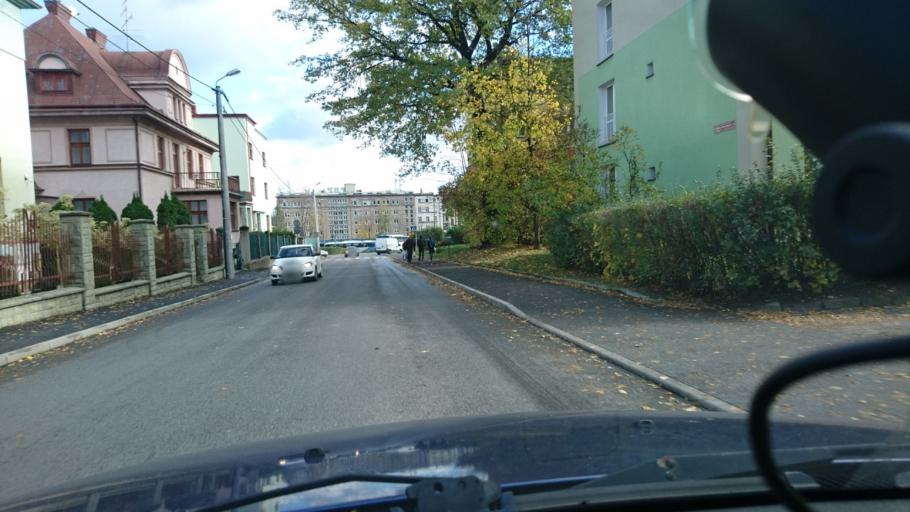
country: PL
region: Silesian Voivodeship
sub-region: Bielsko-Biala
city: Bielsko-Biala
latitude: 49.8296
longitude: 19.0409
